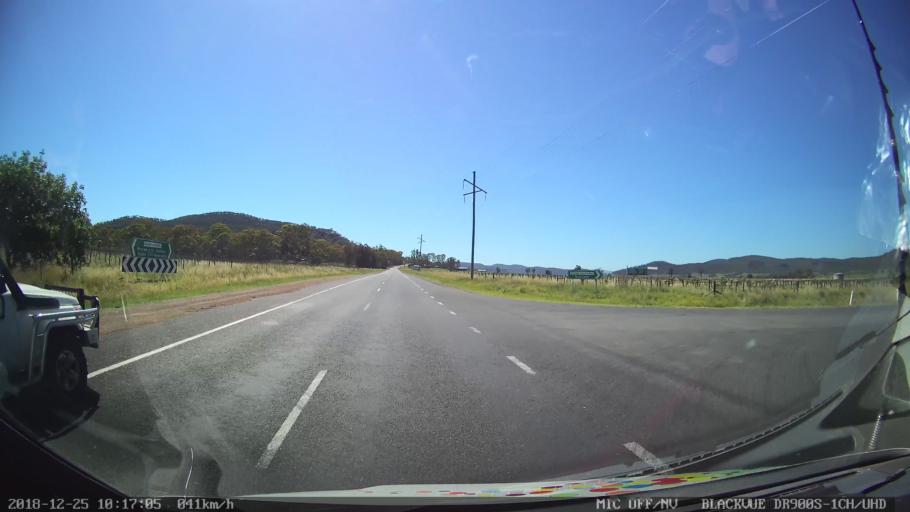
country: AU
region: New South Wales
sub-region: Muswellbrook
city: Denman
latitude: -32.3413
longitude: 150.5812
